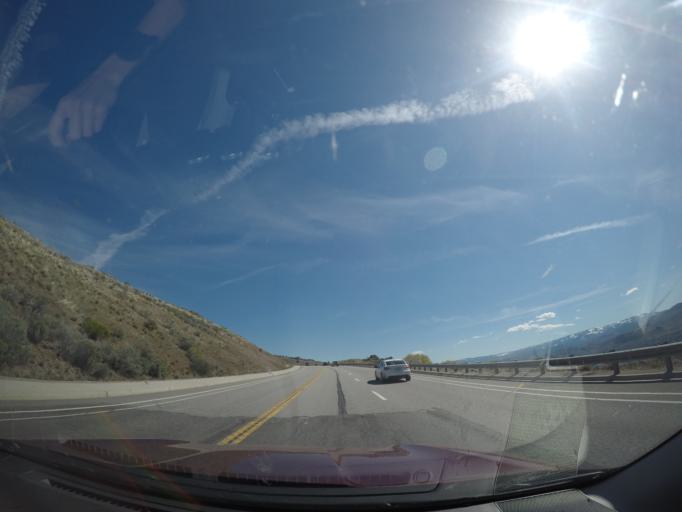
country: US
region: Washington
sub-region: Douglas County
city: East Wenatchee Bench
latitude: 47.4623
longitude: -120.2938
